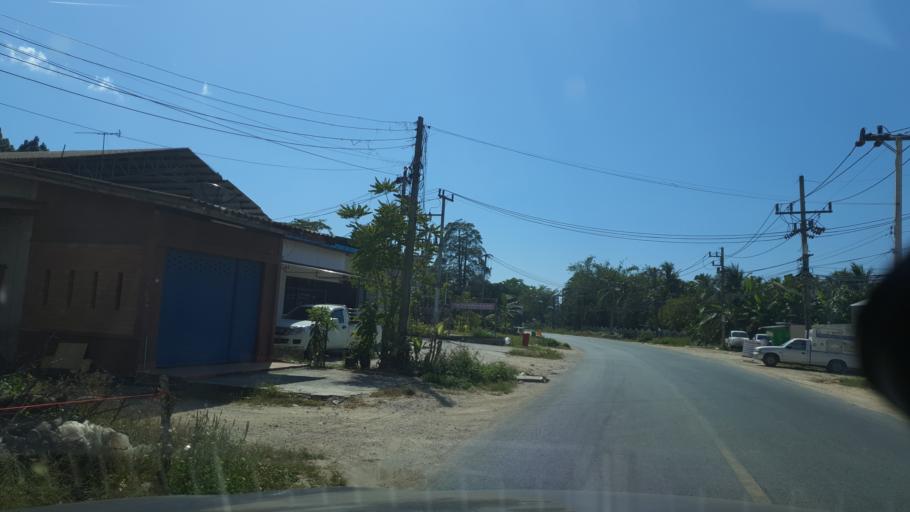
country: TH
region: Phangnga
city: Ban Khao Lak
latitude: 8.5908
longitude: 98.2534
